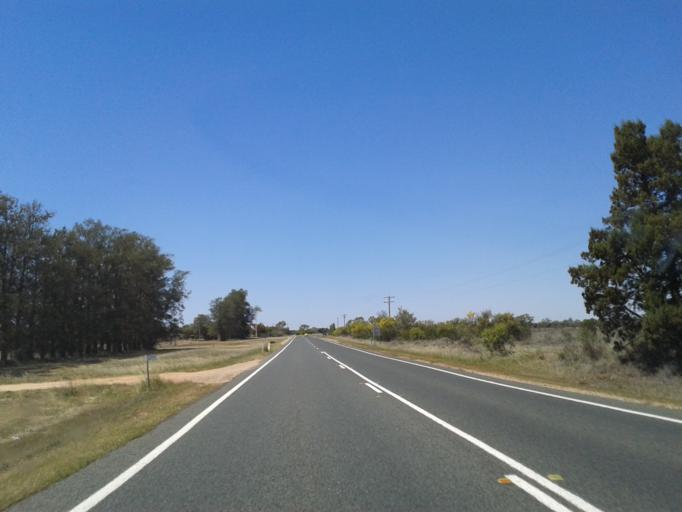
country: AU
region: Victoria
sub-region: Mildura Shire
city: Mildura
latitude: -34.1458
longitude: 142.1750
